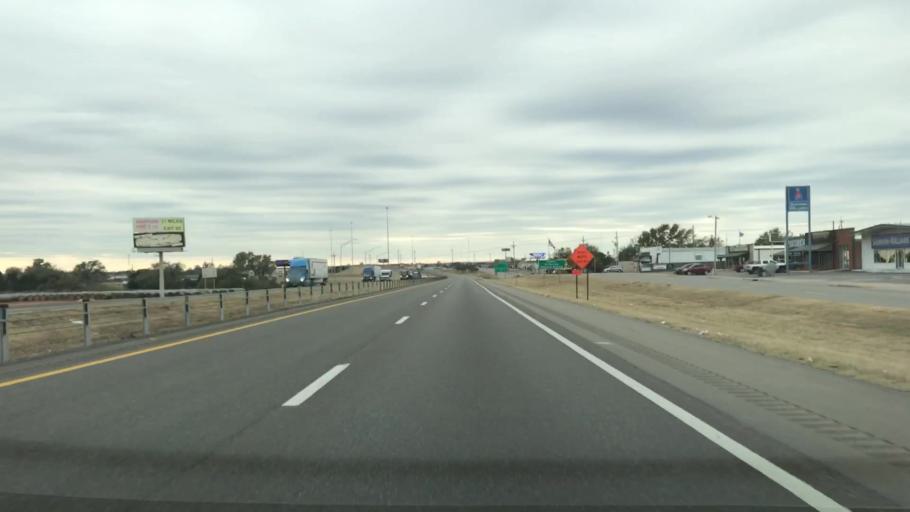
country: US
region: Oklahoma
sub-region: Custer County
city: Weatherford
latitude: 35.5330
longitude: -98.6828
